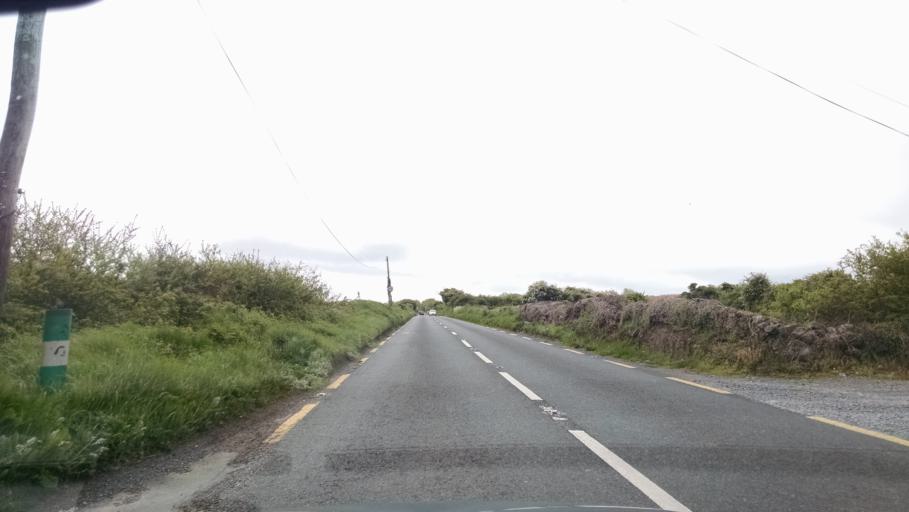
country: IE
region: Connaught
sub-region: County Galway
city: Claregalway
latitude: 53.3706
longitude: -9.0166
